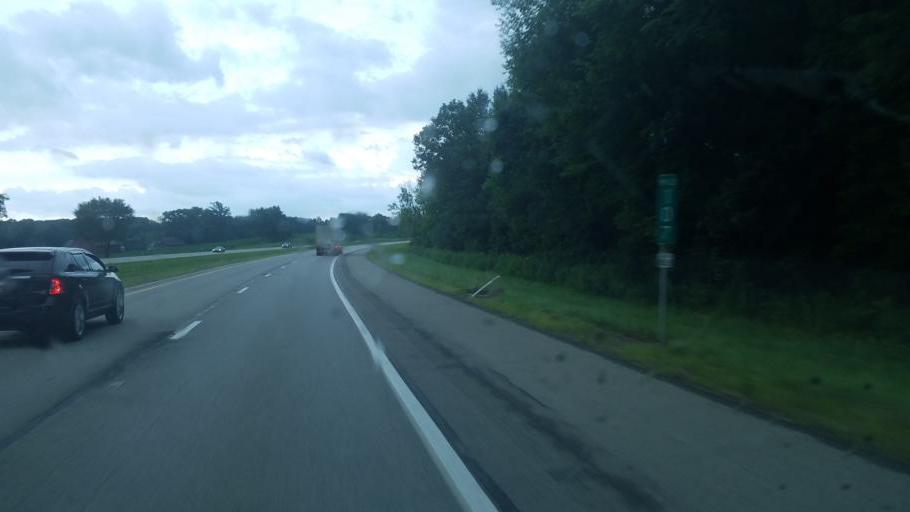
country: US
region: Pennsylvania
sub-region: Butler County
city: Slippery Rock
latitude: 41.0674
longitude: -80.1233
